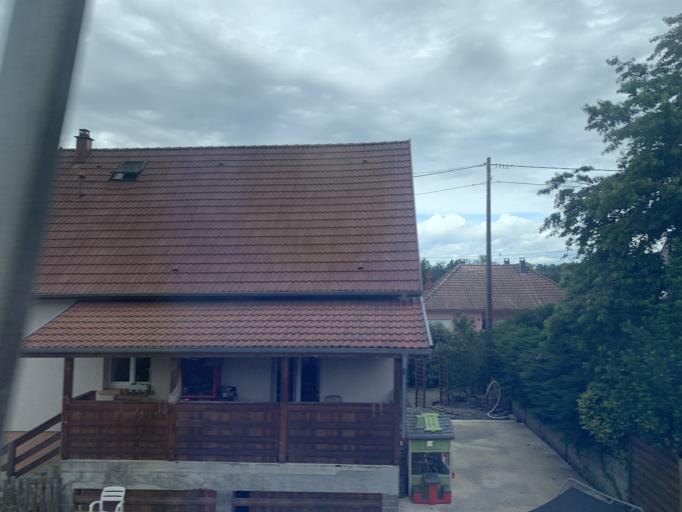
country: FR
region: Alsace
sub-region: Departement du Haut-Rhin
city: Zillisheim
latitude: 47.6924
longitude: 7.2866
